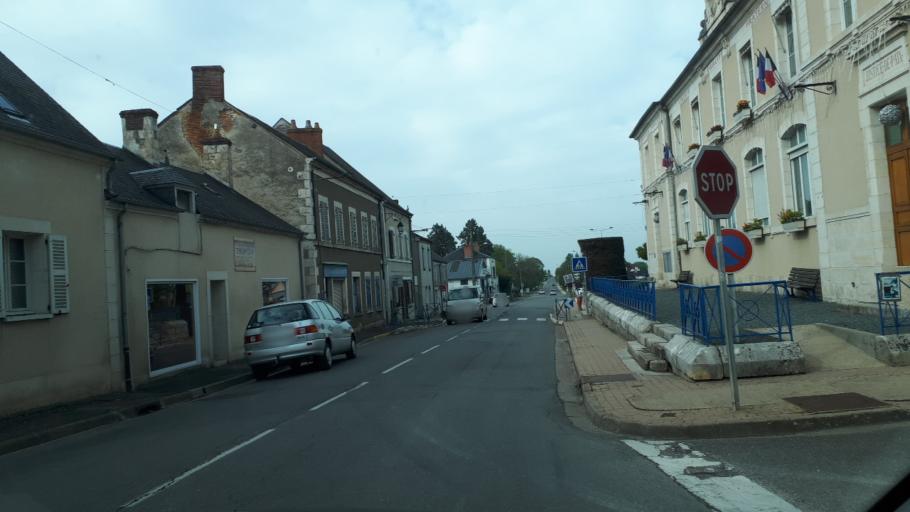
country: FR
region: Centre
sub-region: Departement du Cher
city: Rians
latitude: 47.1979
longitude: 2.5717
